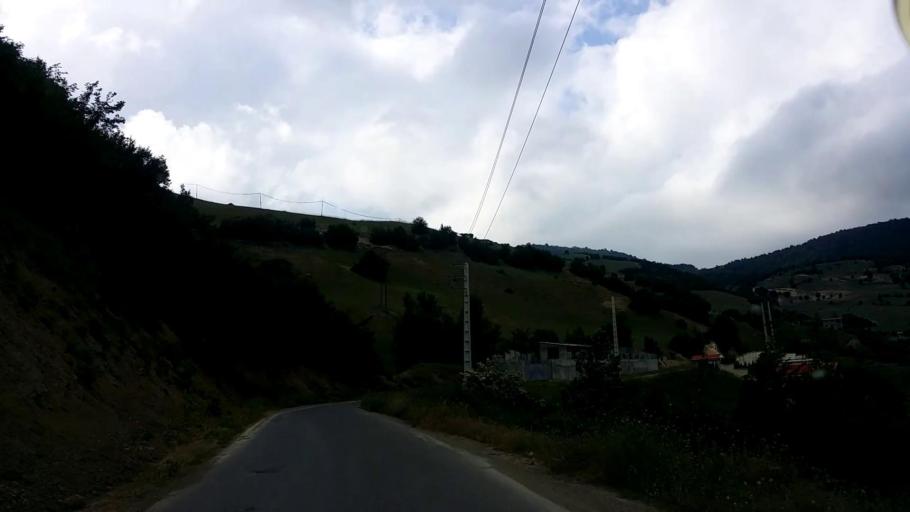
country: IR
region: Mazandaran
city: Chalus
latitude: 36.5492
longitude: 51.2703
